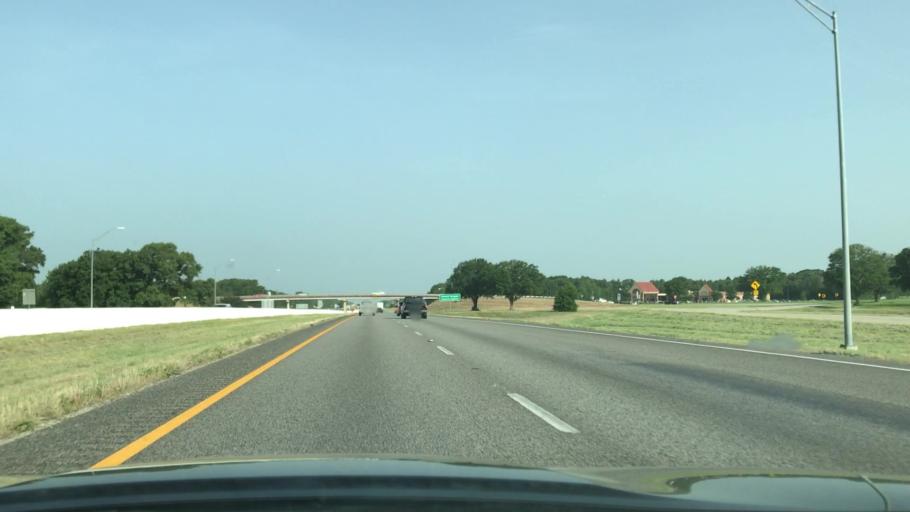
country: US
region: Texas
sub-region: Van Zandt County
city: Canton
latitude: 32.5847
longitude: -95.8703
